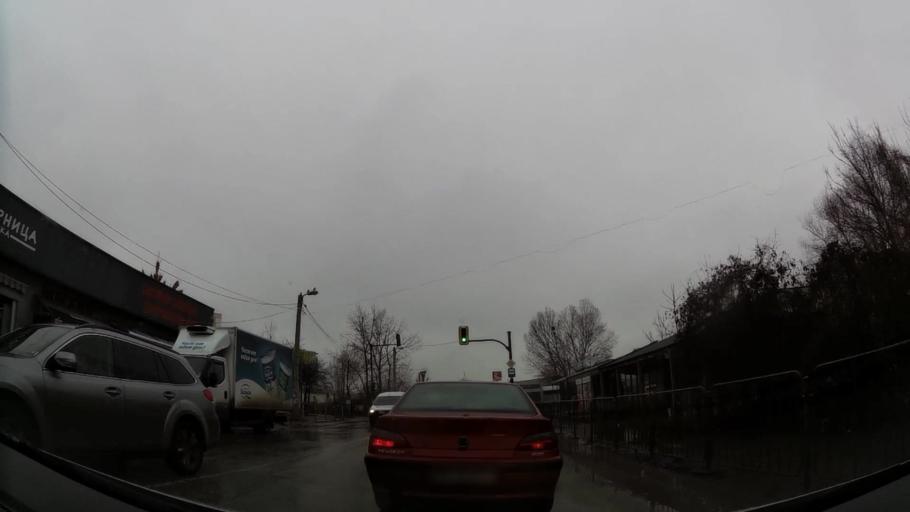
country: BG
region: Sofia-Capital
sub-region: Stolichna Obshtina
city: Sofia
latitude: 42.6432
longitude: 23.4124
